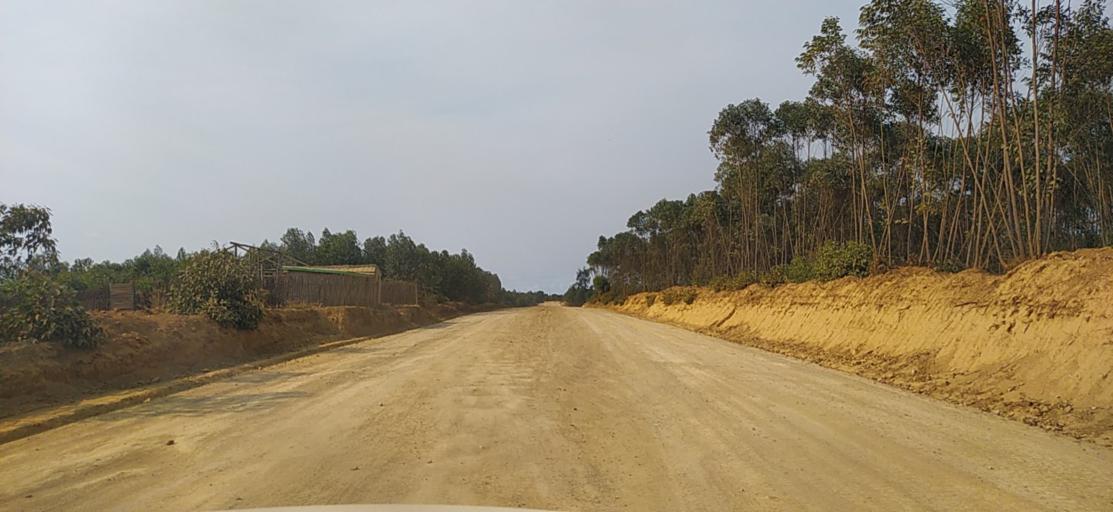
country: MG
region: Alaotra Mangoro
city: Moramanga
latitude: -18.6611
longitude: 48.2738
